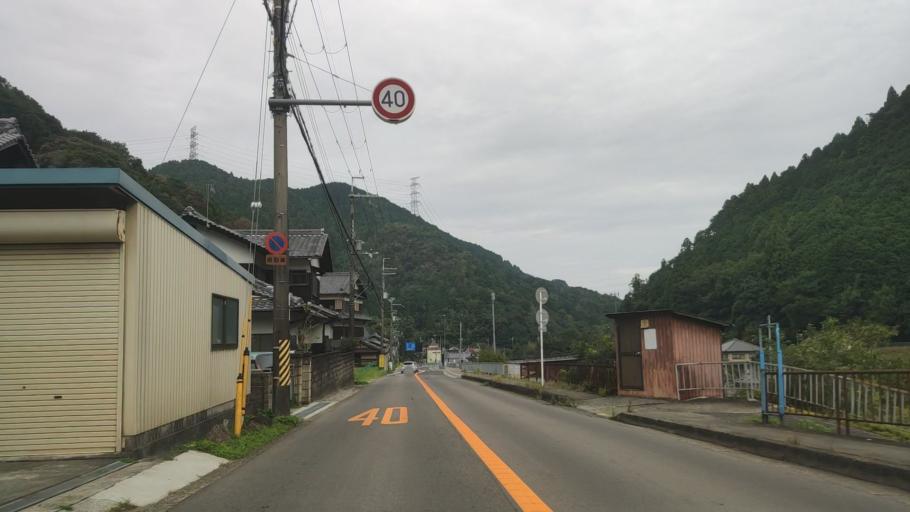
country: JP
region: Wakayama
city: Hashimoto
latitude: 34.3924
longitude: 135.5975
